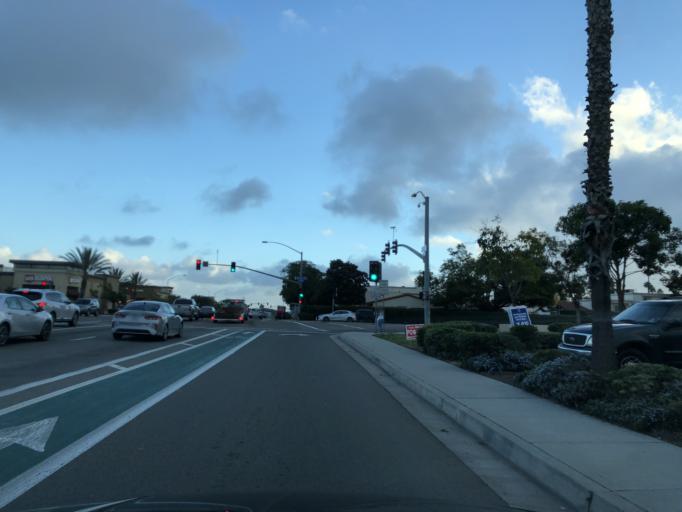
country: US
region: California
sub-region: San Diego County
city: La Jolla
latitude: 32.8198
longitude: -117.1823
